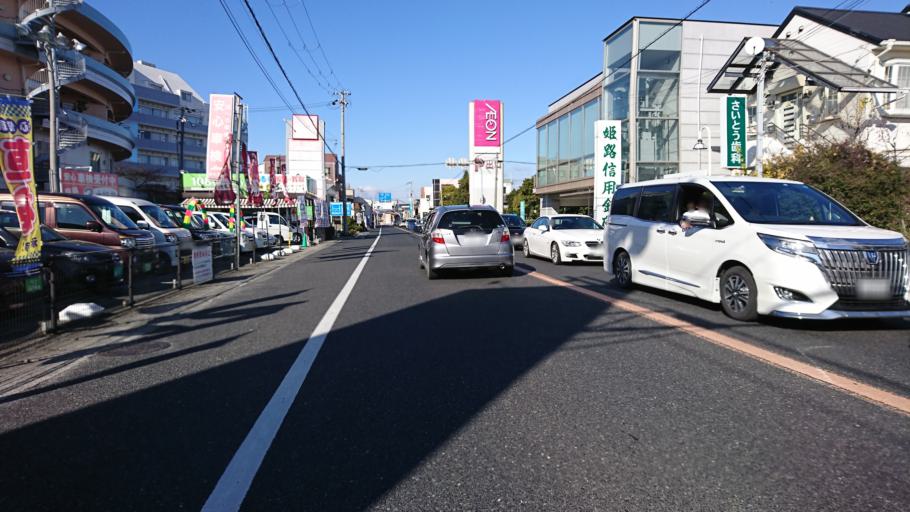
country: JP
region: Hyogo
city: Kakogawacho-honmachi
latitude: 34.7203
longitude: 134.8925
